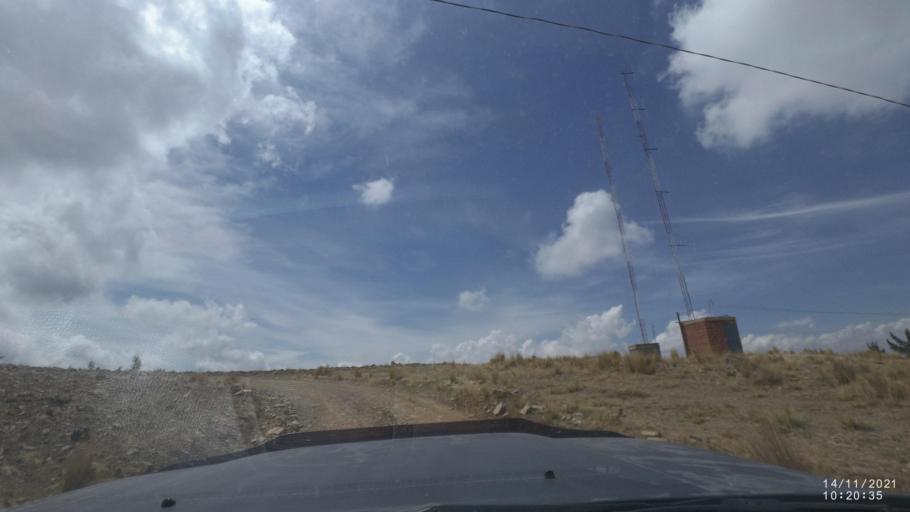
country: BO
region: Cochabamba
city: Cochabamba
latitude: -17.3343
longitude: -66.0814
